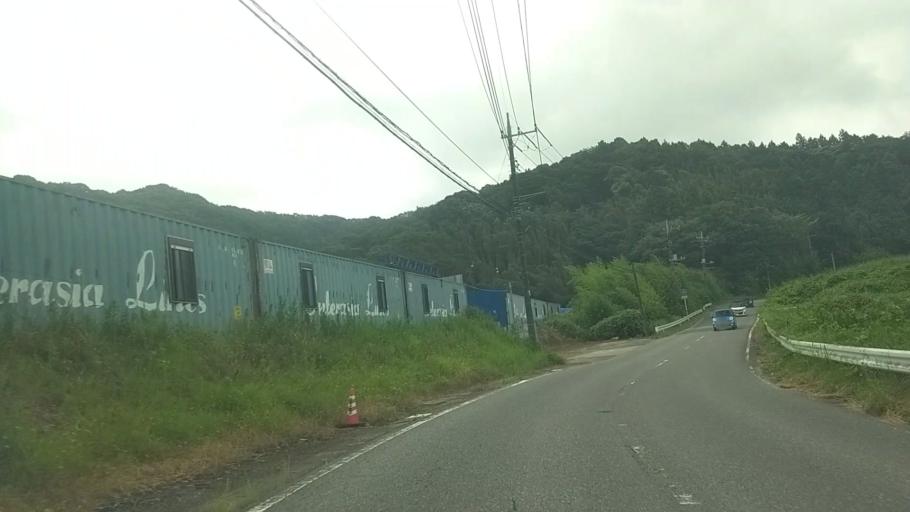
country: JP
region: Chiba
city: Kimitsu
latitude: 35.2325
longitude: 140.0078
